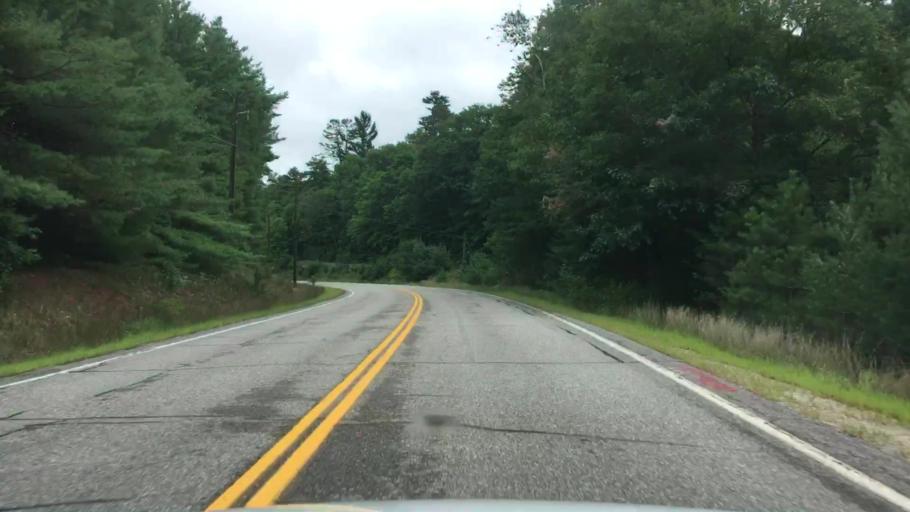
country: US
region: Maine
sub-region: Oxford County
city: Hiram
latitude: 43.8920
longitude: -70.8222
